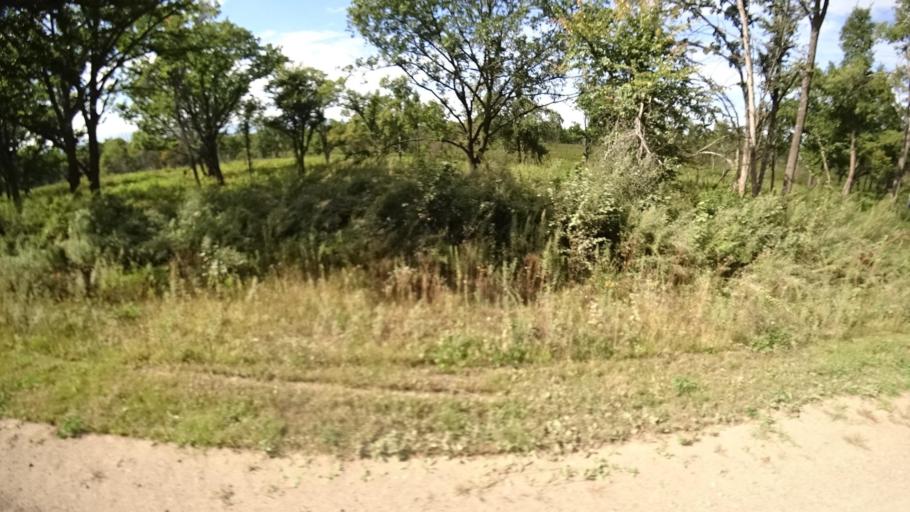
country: RU
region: Primorskiy
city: Yakovlevka
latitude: 44.3969
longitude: 133.5602
